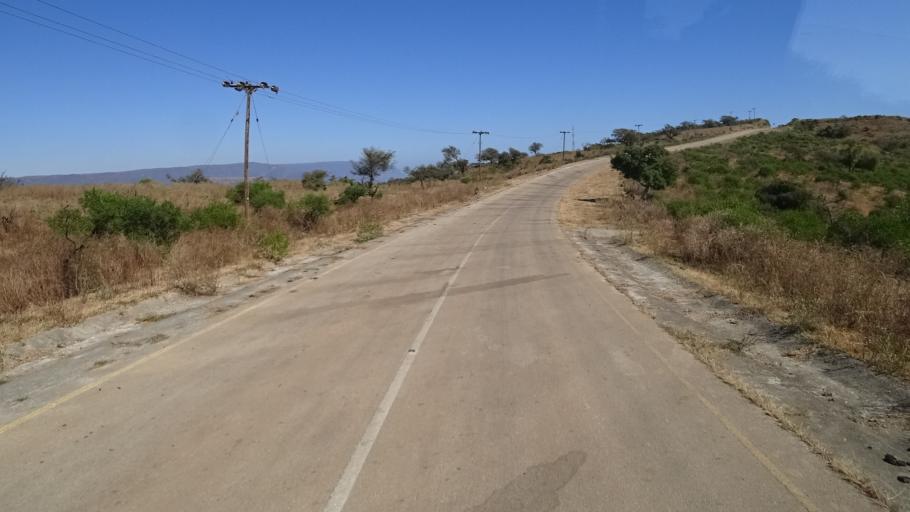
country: YE
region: Al Mahrah
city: Hawf
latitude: 16.7450
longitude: 53.3580
